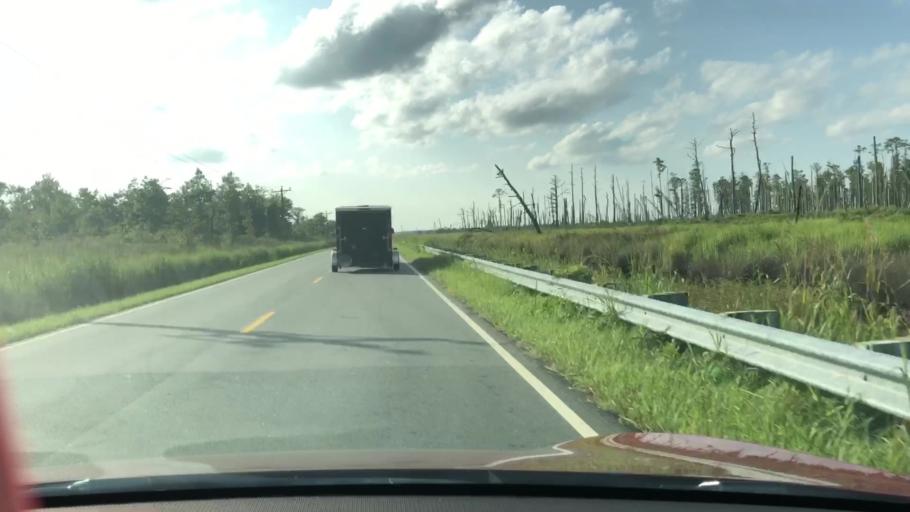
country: US
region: North Carolina
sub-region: Dare County
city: Wanchese
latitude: 35.6202
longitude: -75.8378
